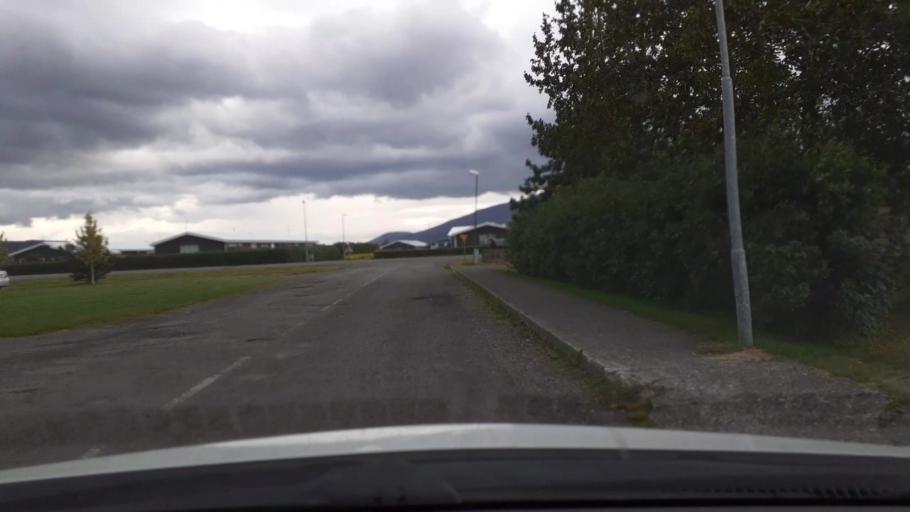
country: IS
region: West
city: Borgarnes
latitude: 64.5624
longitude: -21.7617
